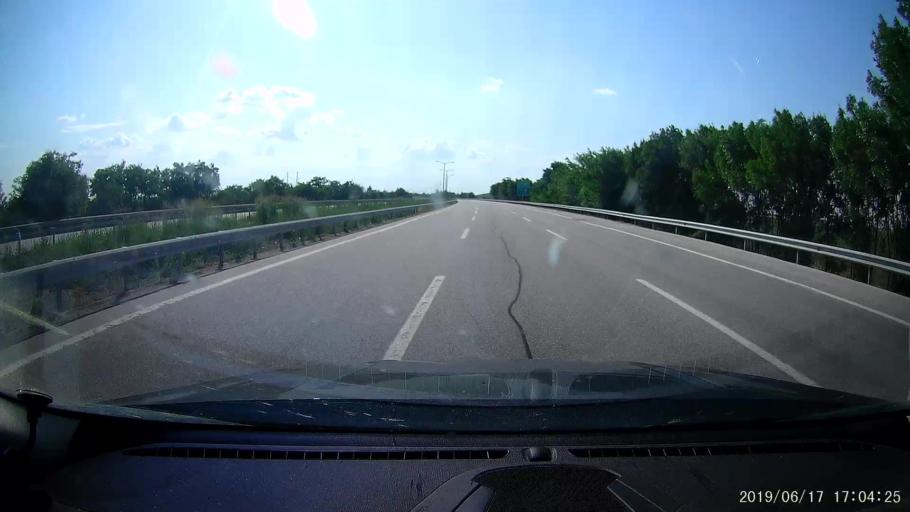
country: TR
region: Edirne
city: Haskoy
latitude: 41.6550
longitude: 26.7281
